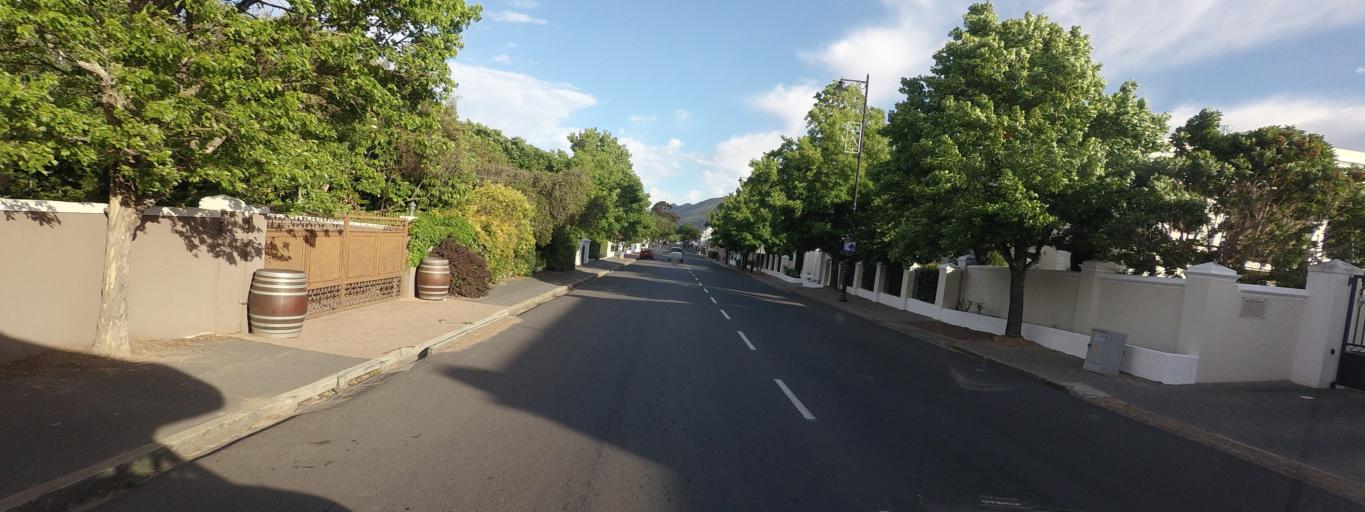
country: ZA
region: Western Cape
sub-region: Cape Winelands District Municipality
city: Paarl
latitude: -33.9137
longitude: 19.1221
